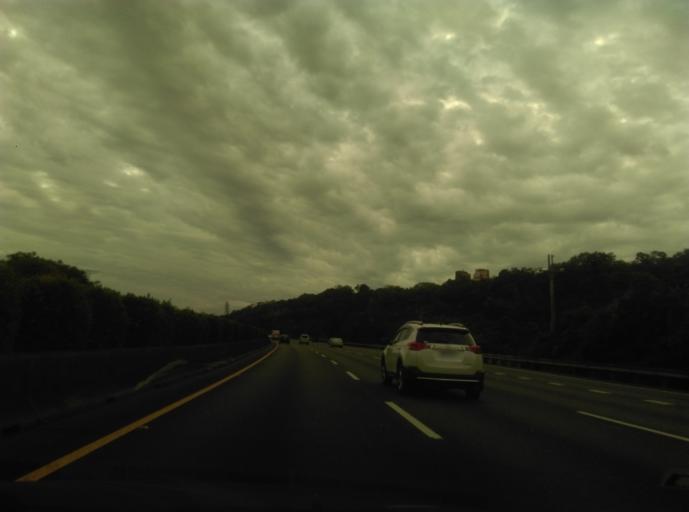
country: TW
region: Taiwan
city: Daxi
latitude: 24.9213
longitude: 121.2987
